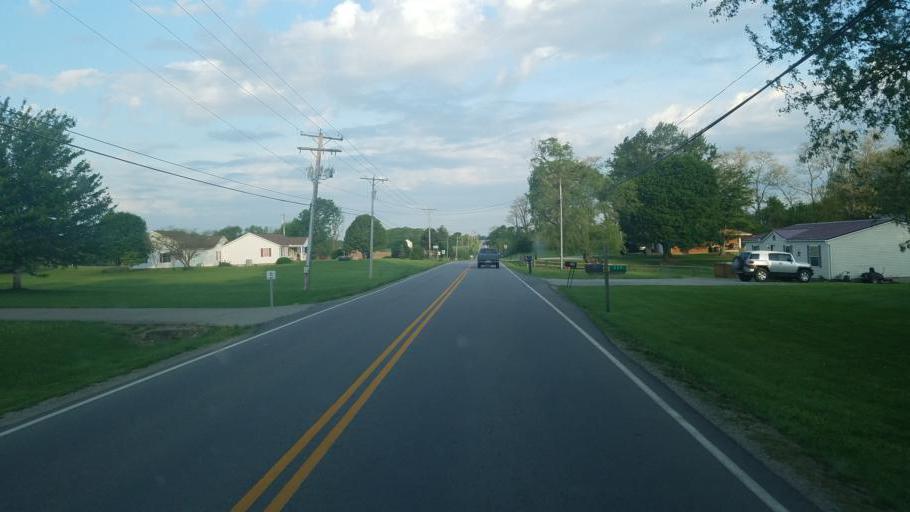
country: US
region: Ohio
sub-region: Highland County
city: Leesburg
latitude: 39.3464
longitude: -83.5691
